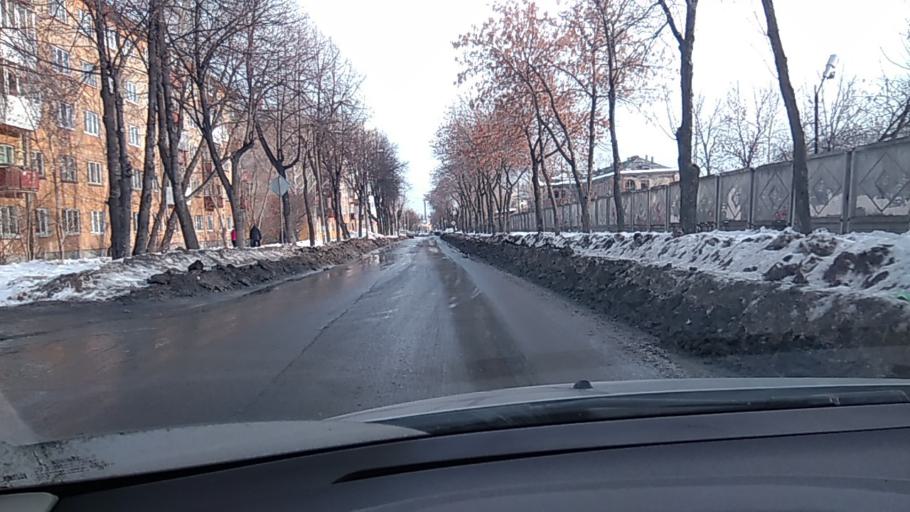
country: RU
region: Sverdlovsk
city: Yekaterinburg
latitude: 56.8892
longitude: 60.5732
